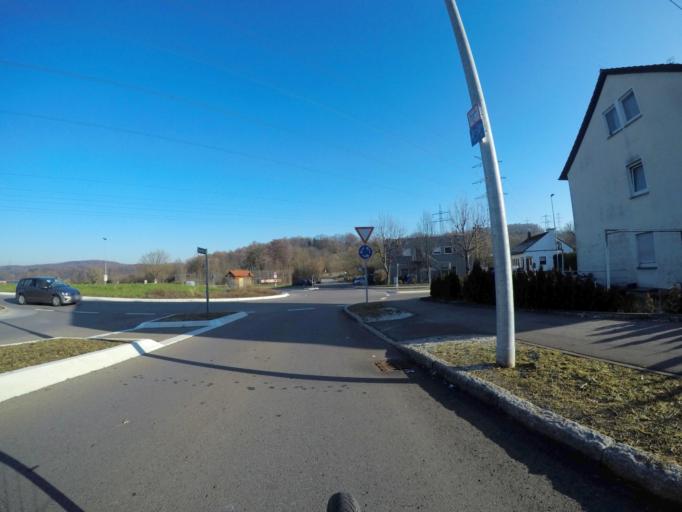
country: DE
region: Baden-Wuerttemberg
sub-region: Tuebingen Region
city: Pliezhausen
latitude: 48.5254
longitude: 9.2278
